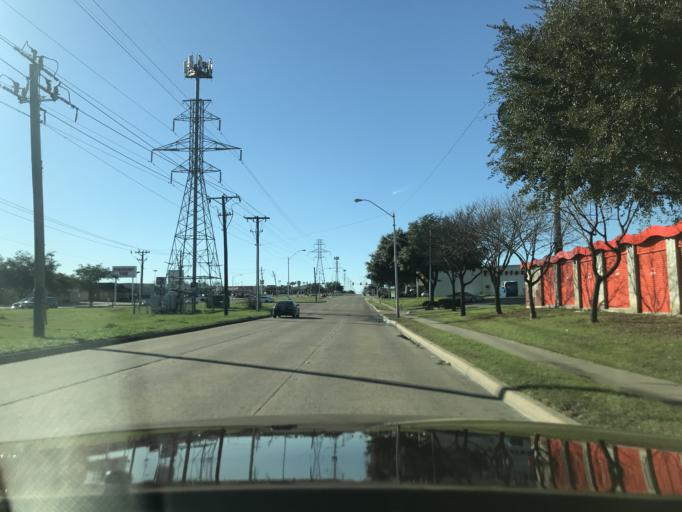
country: US
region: Texas
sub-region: Tarrant County
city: Edgecliff Village
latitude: 32.6493
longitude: -97.3623
